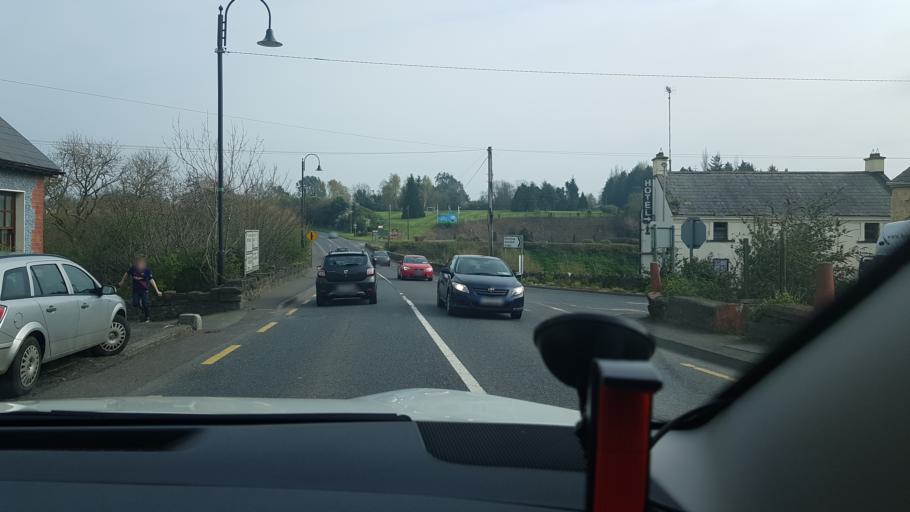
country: IE
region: Leinster
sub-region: An Mhi
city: Stamullin
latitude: 53.6716
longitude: -6.2845
